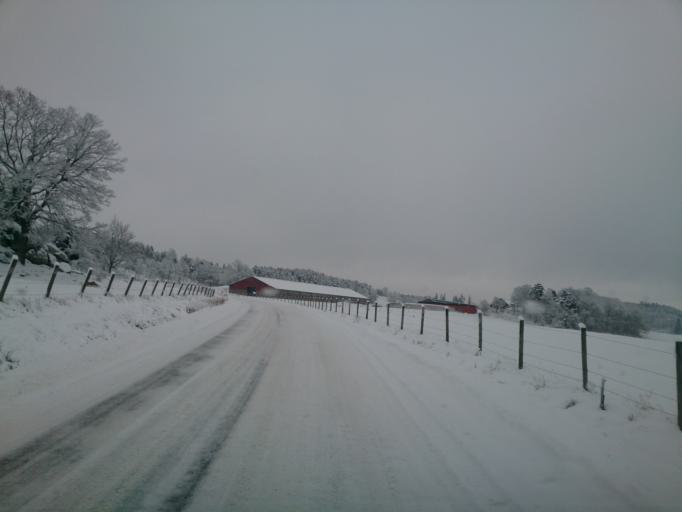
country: SE
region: OEstergoetland
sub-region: Atvidabergs Kommun
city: Atvidaberg
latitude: 58.2936
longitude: 15.8850
